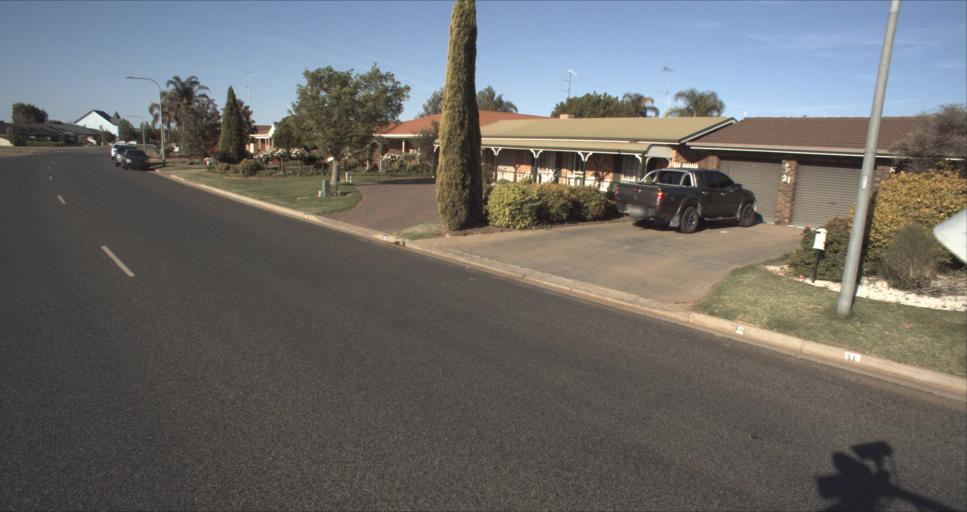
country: AU
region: New South Wales
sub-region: Leeton
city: Leeton
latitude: -34.5425
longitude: 146.3999
